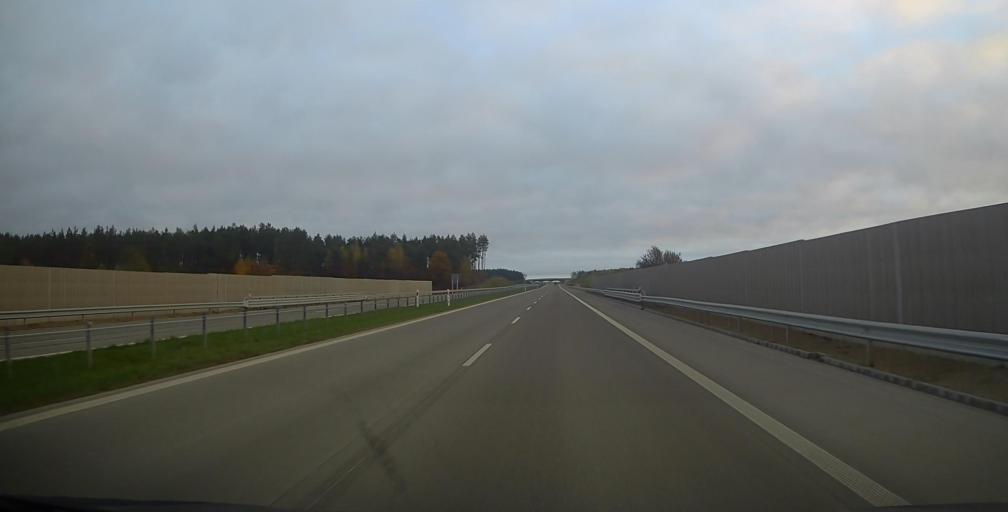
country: PL
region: Podlasie
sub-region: Powiat lomzynski
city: Piatnica
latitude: 53.2772
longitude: 22.1327
